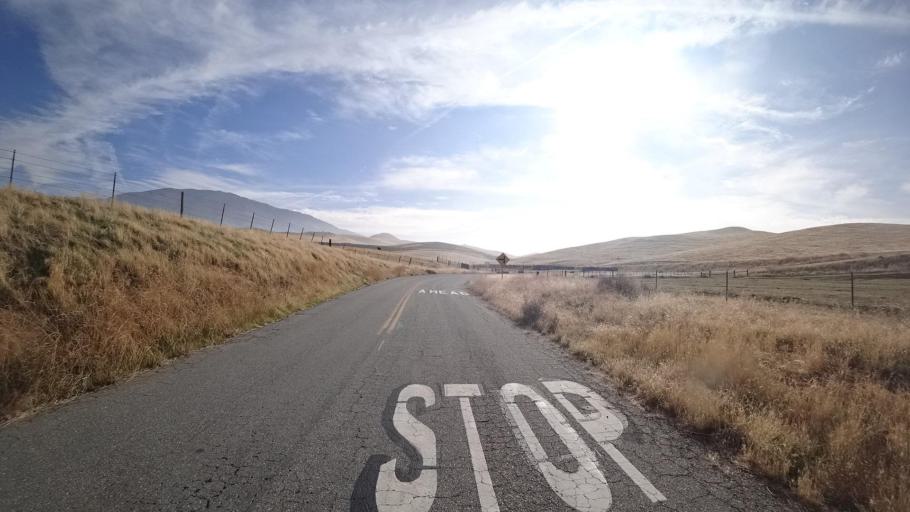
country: US
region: California
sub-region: Kern County
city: Bear Valley Springs
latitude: 35.2769
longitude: -118.6881
